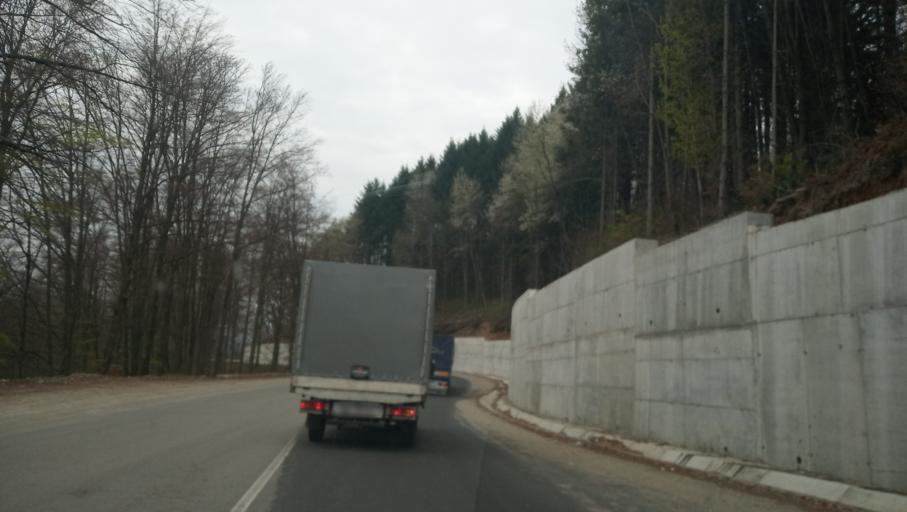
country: RO
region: Bihor
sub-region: Comuna Cristioru de Jos
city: Cristioru de Jos
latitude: 46.3750
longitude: 22.5536
